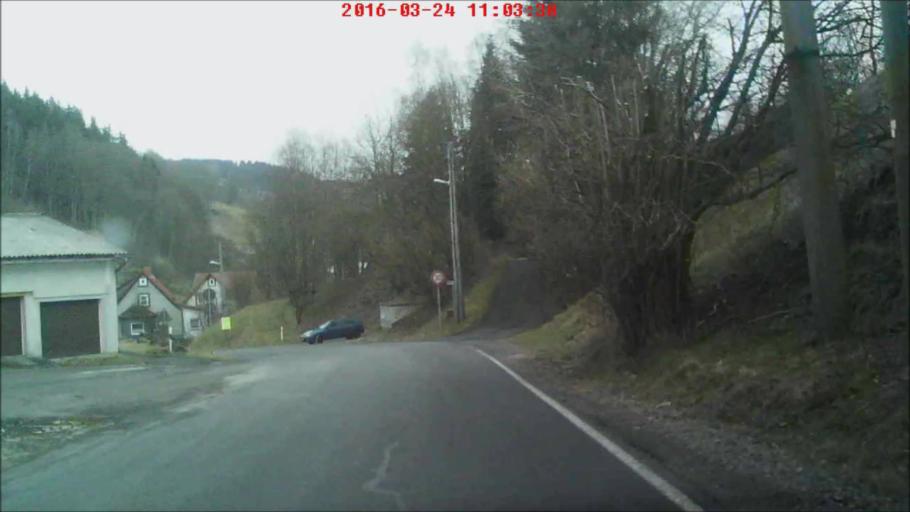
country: DE
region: Thuringia
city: Neustadt am Rennsteig
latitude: 50.5444
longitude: 10.9195
